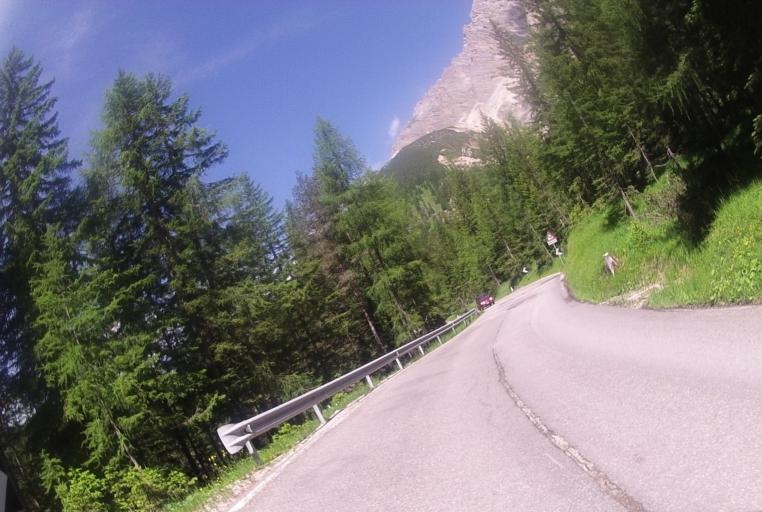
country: IT
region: Veneto
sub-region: Provincia di Belluno
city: Cortina d'Ampezzo
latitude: 46.5568
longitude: 12.2230
